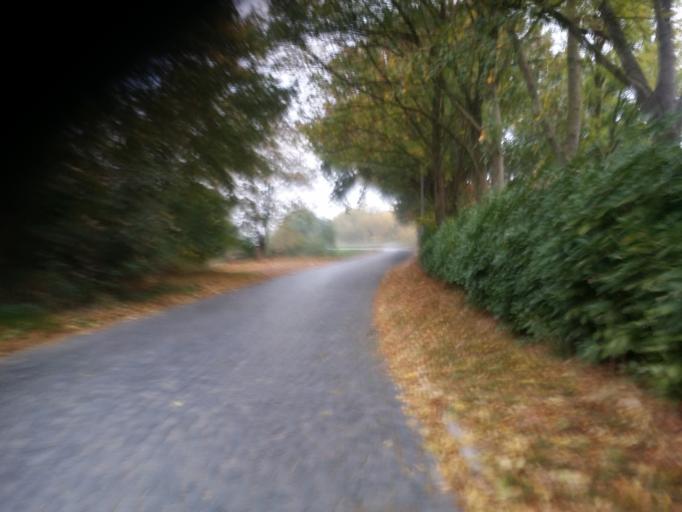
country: DE
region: Lower Saxony
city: Ritterhude
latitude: 53.1650
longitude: 8.7360
